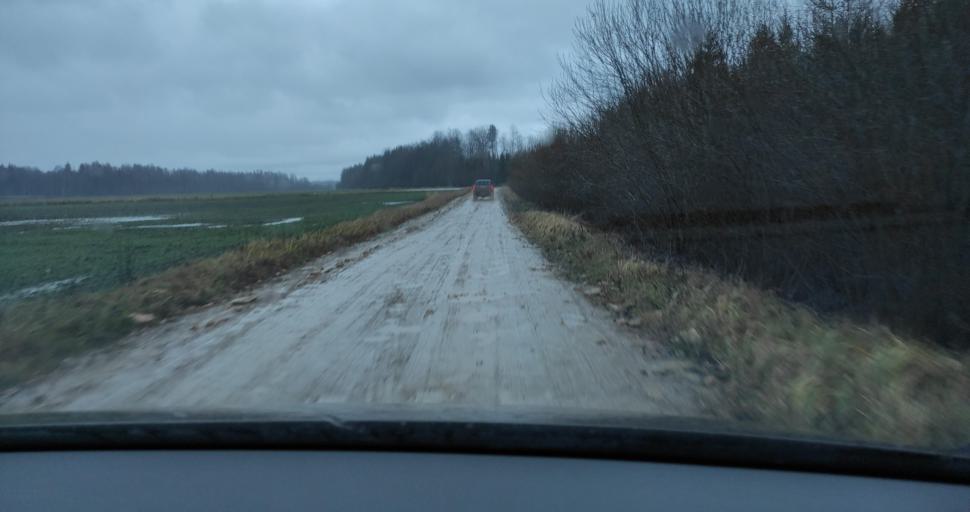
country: LV
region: Skrunda
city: Skrunda
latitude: 56.6248
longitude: 22.2341
